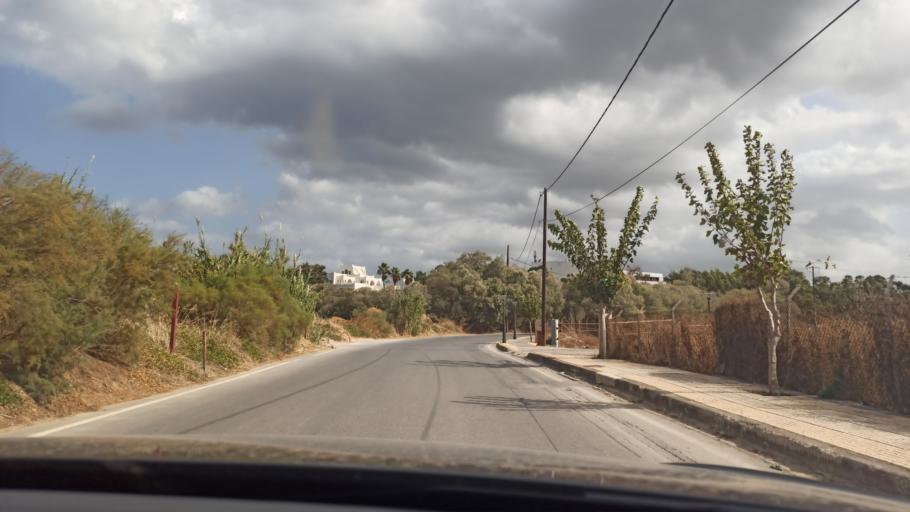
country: GR
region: Crete
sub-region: Nomos Irakleiou
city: Gazi
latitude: 35.3393
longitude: 25.0547
